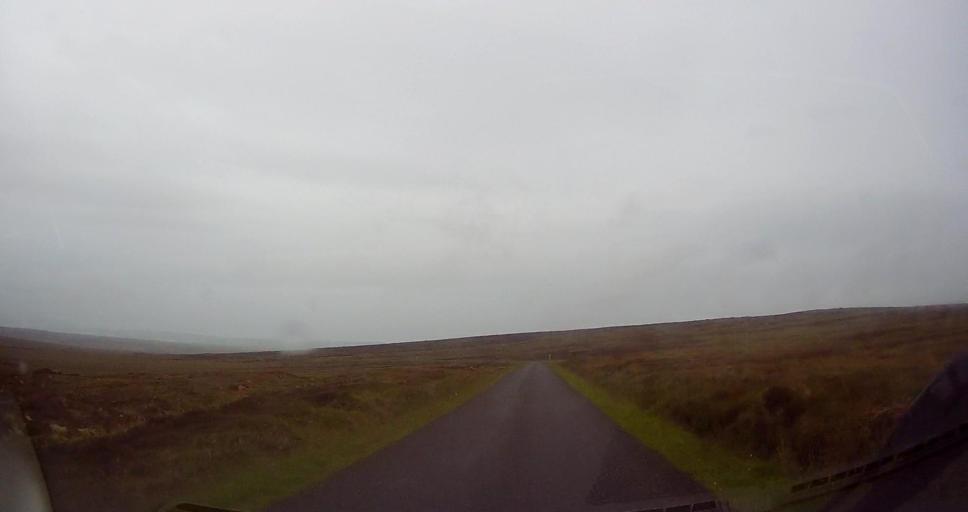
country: GB
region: Scotland
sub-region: Orkney Islands
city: Stromness
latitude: 59.1020
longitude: -3.1412
